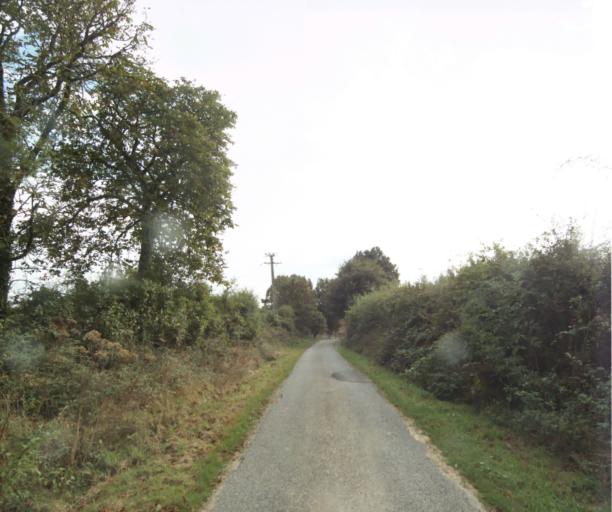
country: FR
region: Bourgogne
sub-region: Departement de Saone-et-Loire
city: Palinges
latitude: 46.5279
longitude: 4.2655
